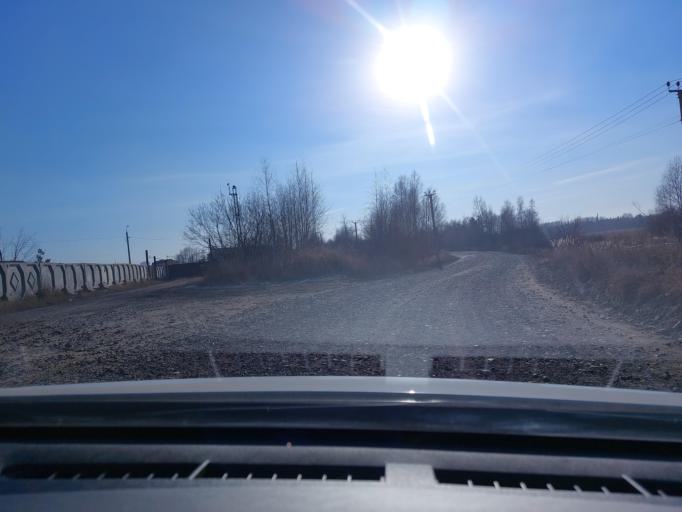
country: RU
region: Irkutsk
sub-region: Irkutskiy Rayon
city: Irkutsk
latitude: 52.3088
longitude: 104.2724
